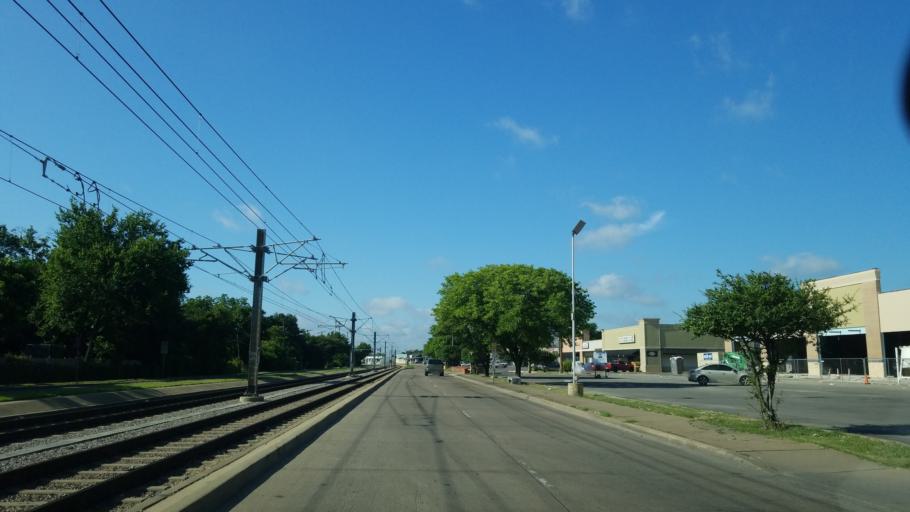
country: US
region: Texas
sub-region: Dallas County
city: Dallas
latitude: 32.7158
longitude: -96.8045
